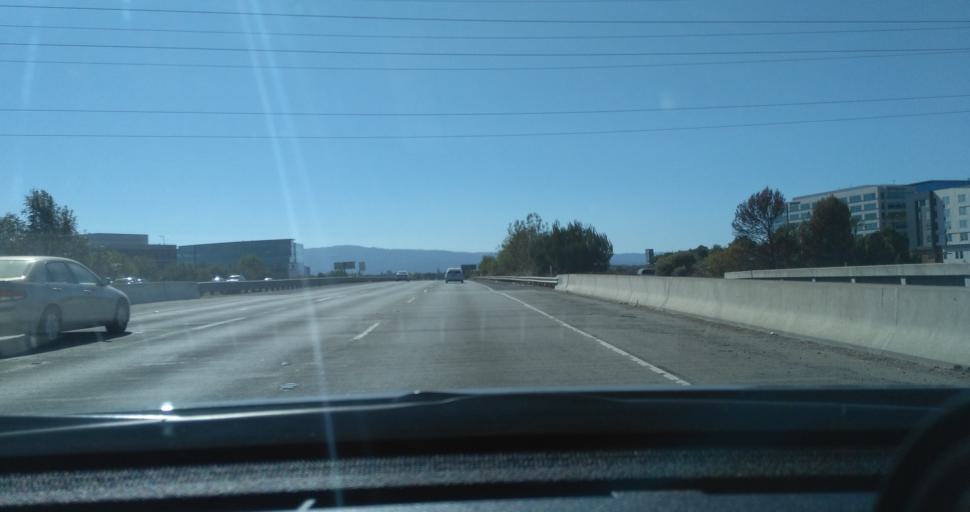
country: US
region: California
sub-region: Santa Clara County
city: Santa Clara
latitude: 37.4175
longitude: -121.9740
